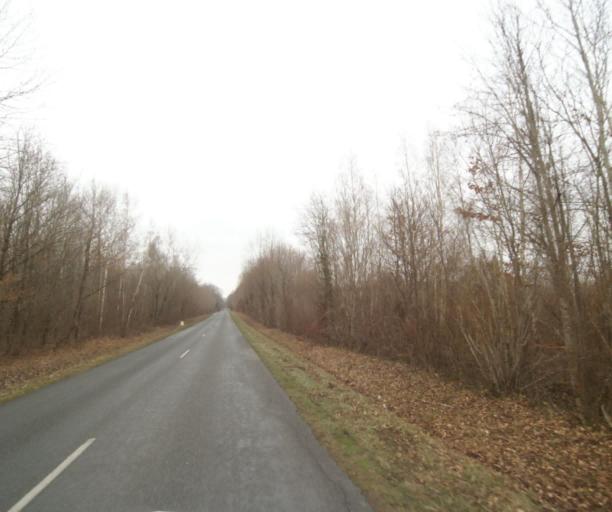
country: FR
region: Champagne-Ardenne
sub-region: Departement de la Marne
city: Pargny-sur-Saulx
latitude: 48.7227
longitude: 4.8741
